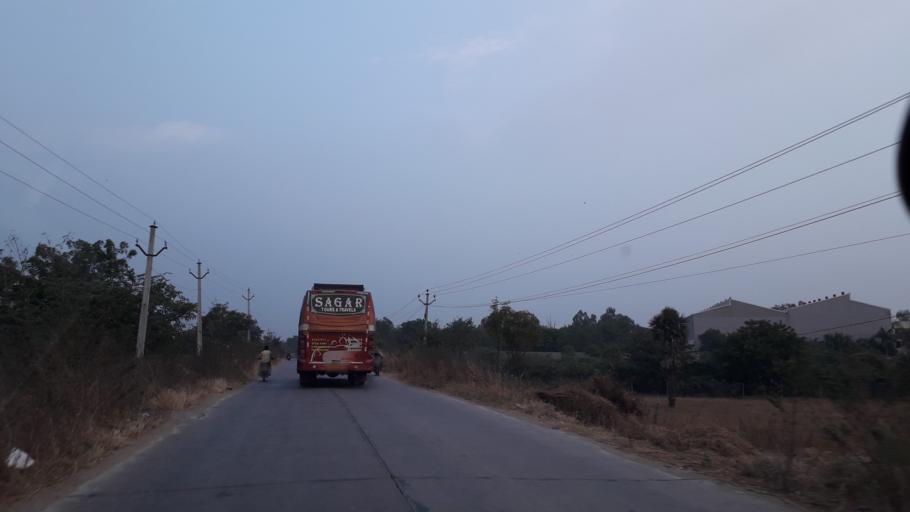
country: IN
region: Telangana
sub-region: Medak
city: Patancheru
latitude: 17.5212
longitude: 78.2426
